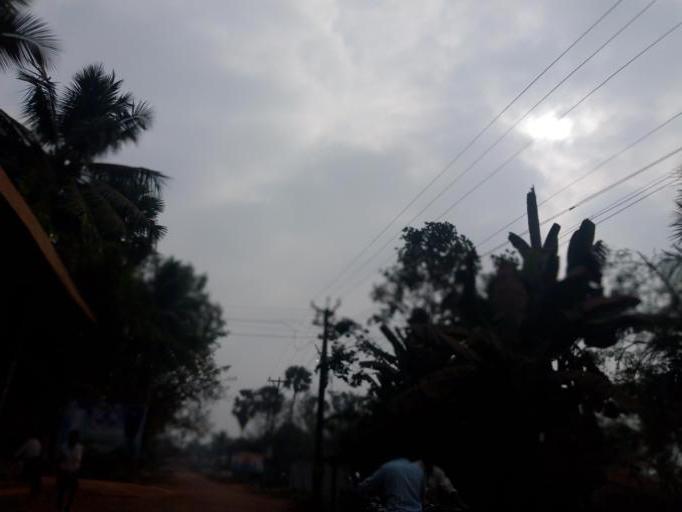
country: IN
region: Andhra Pradesh
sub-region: West Godavari
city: Tadepallegudem
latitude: 16.8633
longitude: 81.3281
